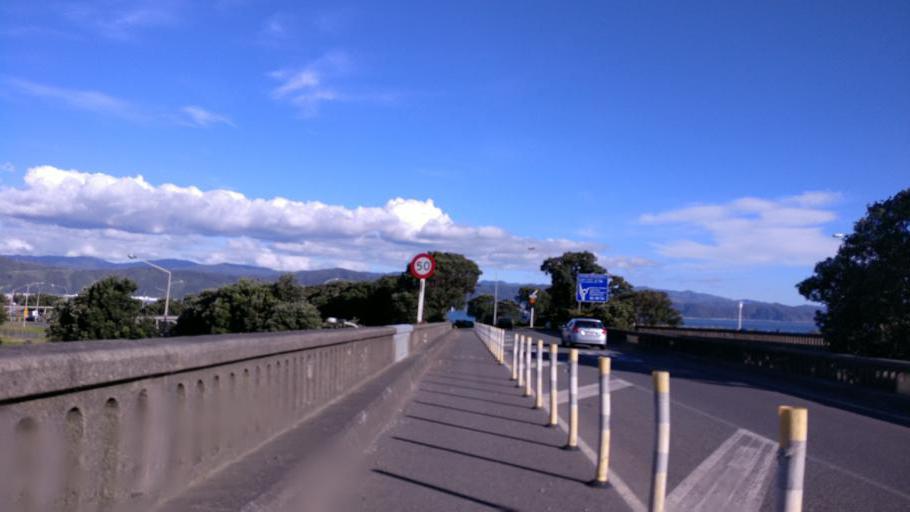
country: NZ
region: Wellington
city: Petone
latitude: -41.2232
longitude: 174.8597
